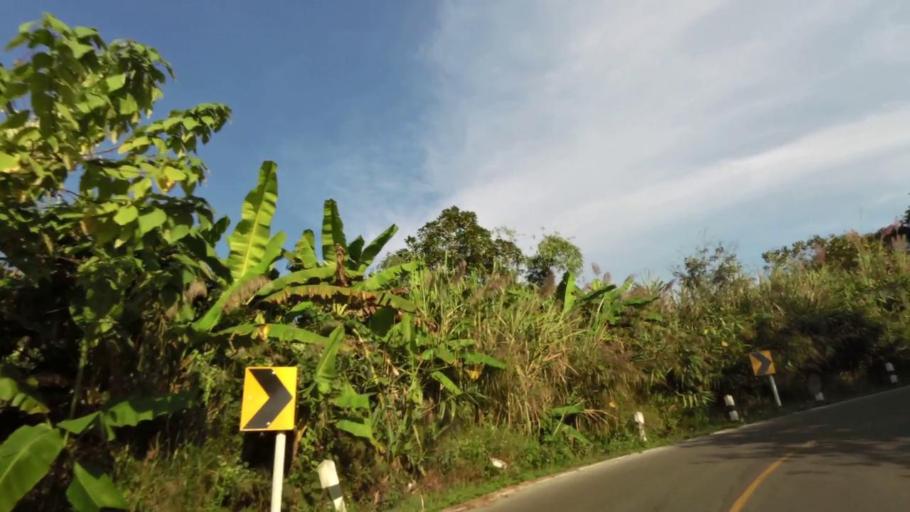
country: TH
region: Chiang Rai
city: Khun Tan
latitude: 19.8495
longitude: 100.4407
